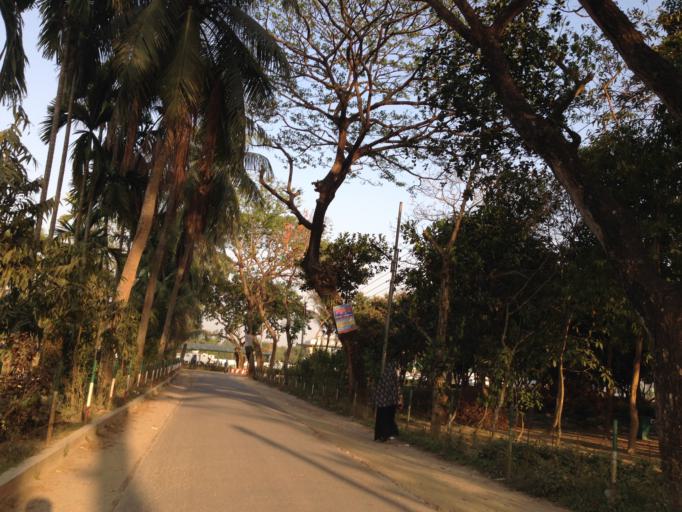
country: BD
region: Dhaka
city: Mirzapur
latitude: 24.1614
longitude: 90.0422
